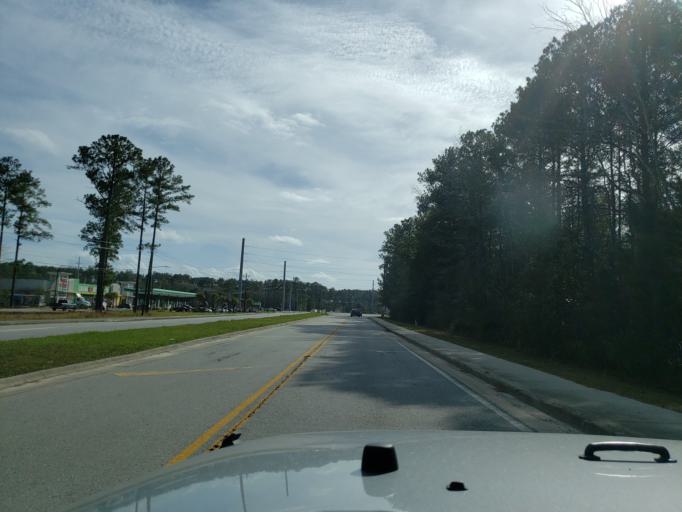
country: US
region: Georgia
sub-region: Chatham County
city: Pooler
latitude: 32.1660
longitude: -81.2338
